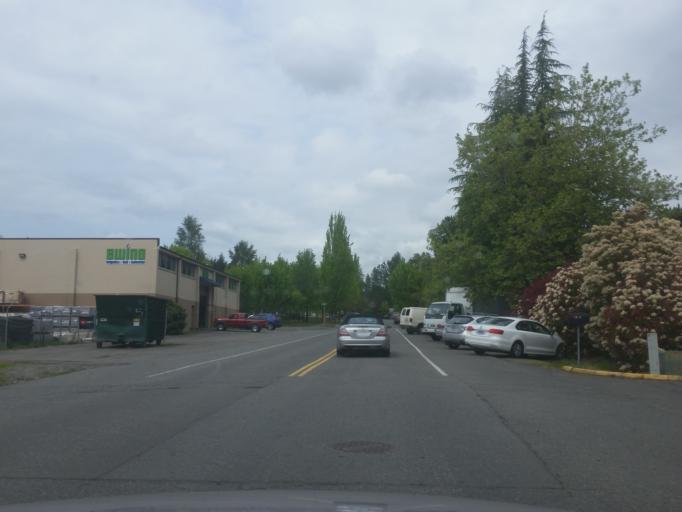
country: US
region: Washington
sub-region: King County
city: Kirkland
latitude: 47.6814
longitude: -122.1932
